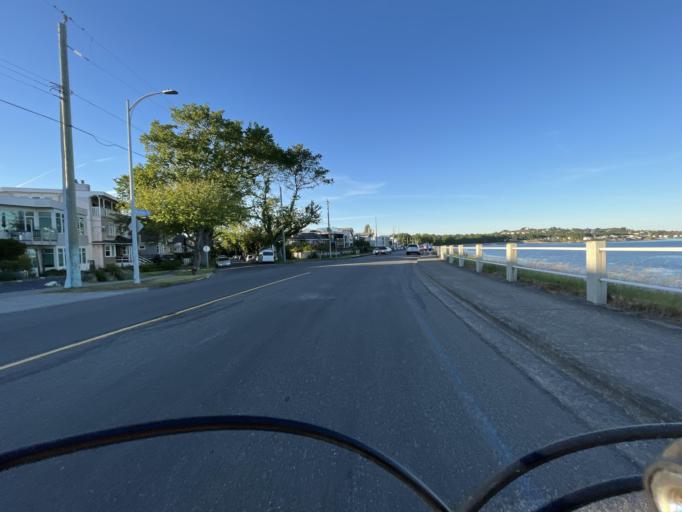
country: CA
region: British Columbia
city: Victoria
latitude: 48.4065
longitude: -123.3490
